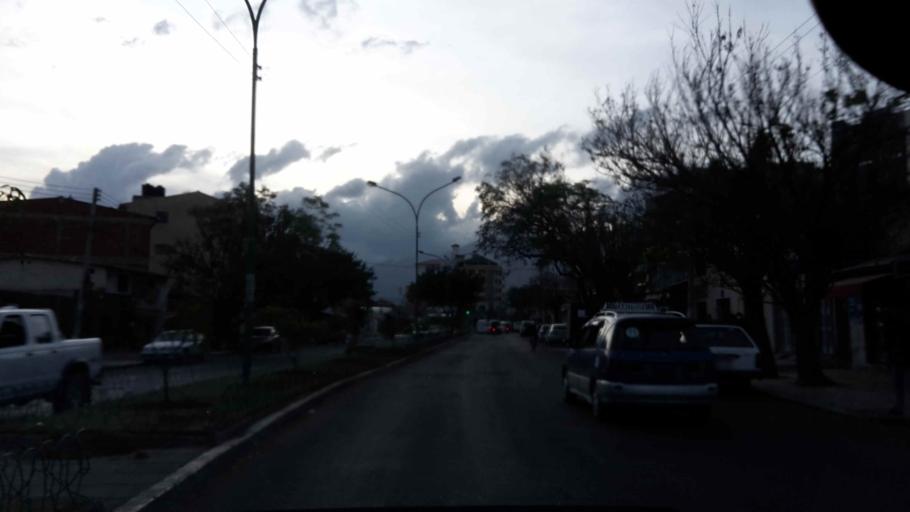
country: BO
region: Cochabamba
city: Cochabamba
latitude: -17.3637
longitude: -66.1789
